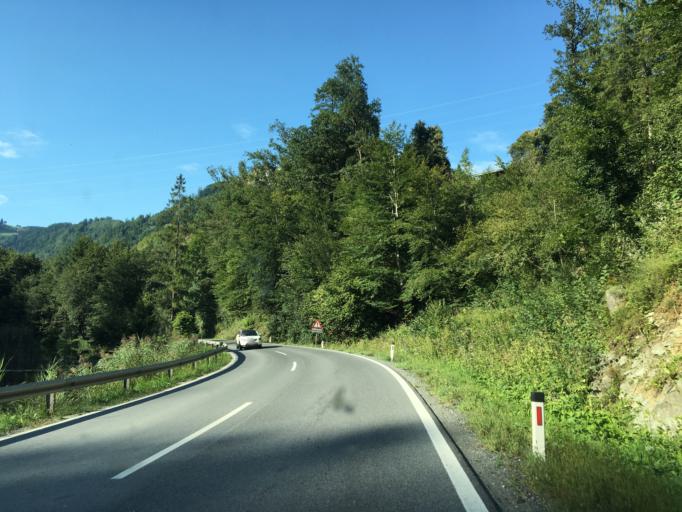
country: AT
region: Carinthia
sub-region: Politischer Bezirk Volkermarkt
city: Diex
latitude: 46.7029
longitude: 14.5684
